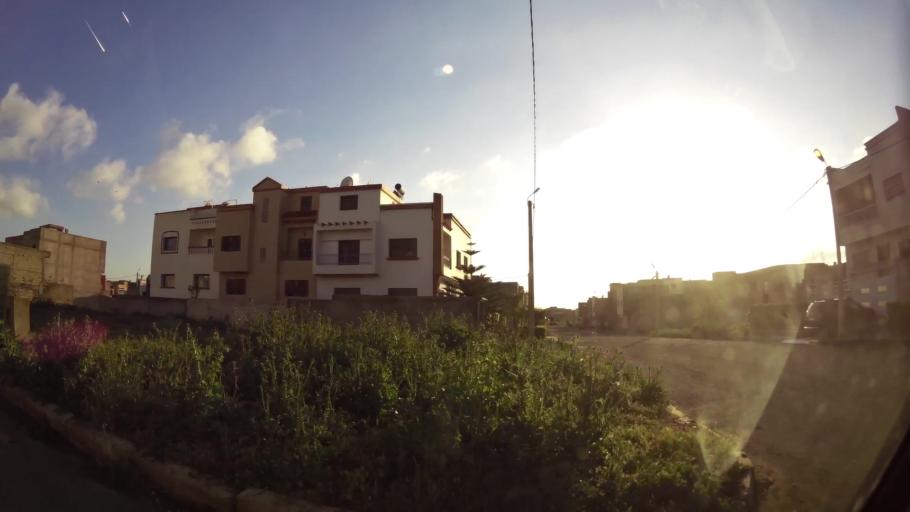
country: MA
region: Chaouia-Ouardigha
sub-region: Settat Province
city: Settat
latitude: 33.0097
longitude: -7.5962
